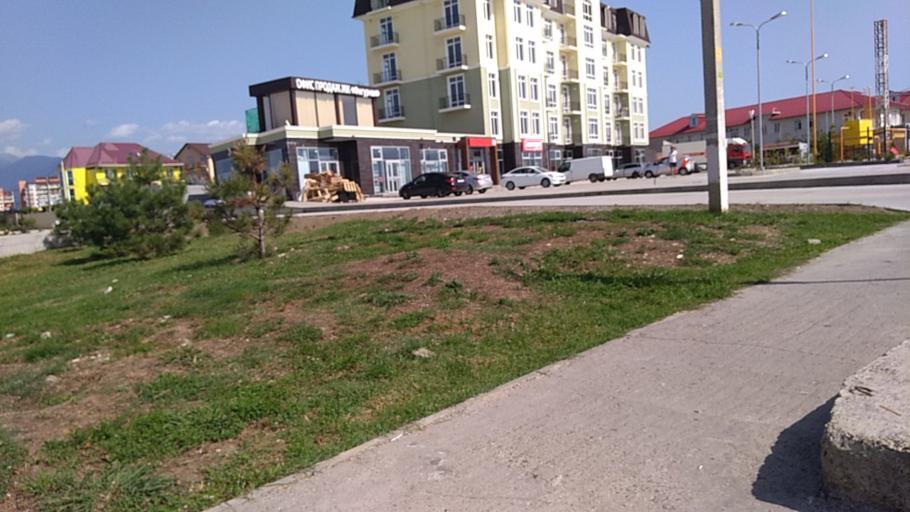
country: RU
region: Krasnodarskiy
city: Vysokoye
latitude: 43.3981
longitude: 39.9950
